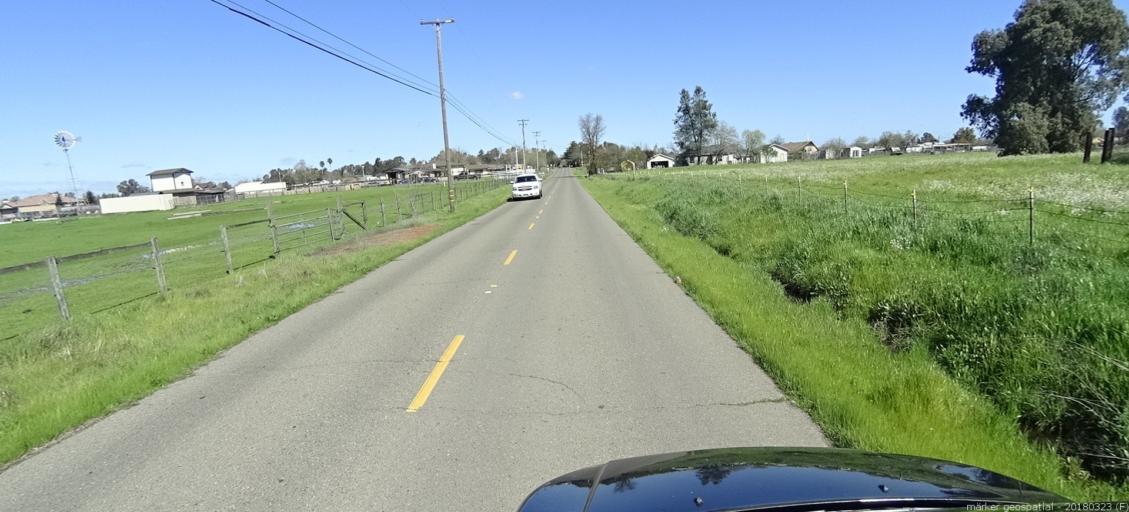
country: US
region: California
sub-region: Sacramento County
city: Rio Linda
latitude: 38.6878
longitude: -121.4198
